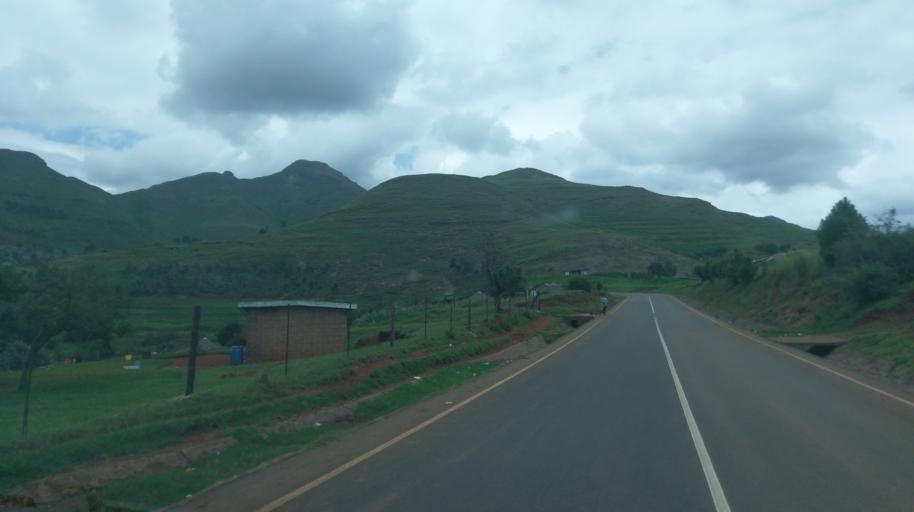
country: LS
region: Butha-Buthe
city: Butha-Buthe
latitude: -29.0332
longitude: 28.2863
